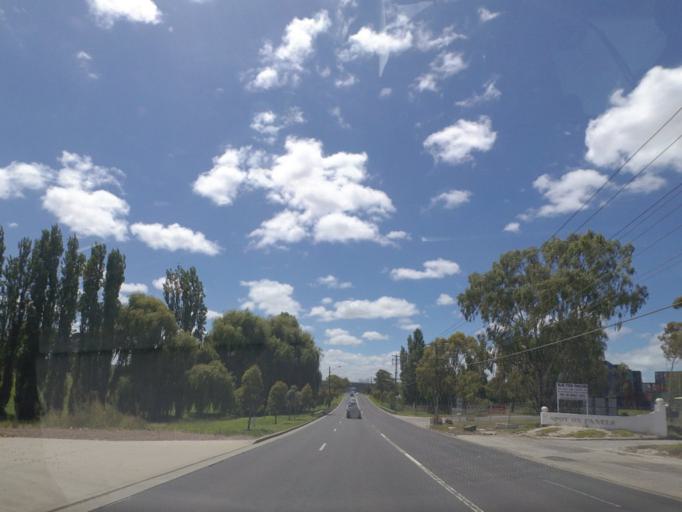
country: AU
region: Victoria
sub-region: Maribyrnong
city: Braybrook
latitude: -37.7971
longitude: 144.8415
